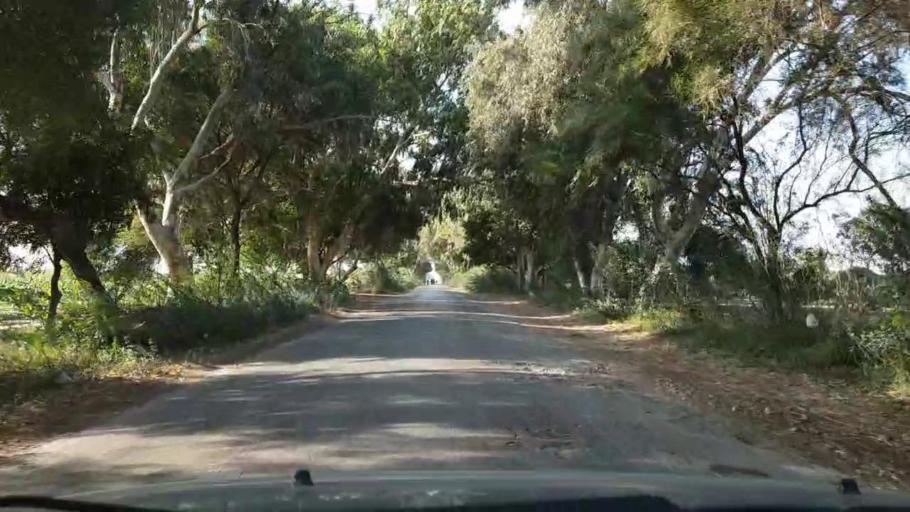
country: PK
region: Sindh
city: Tando Ghulam Ali
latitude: 25.1352
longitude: 68.8790
